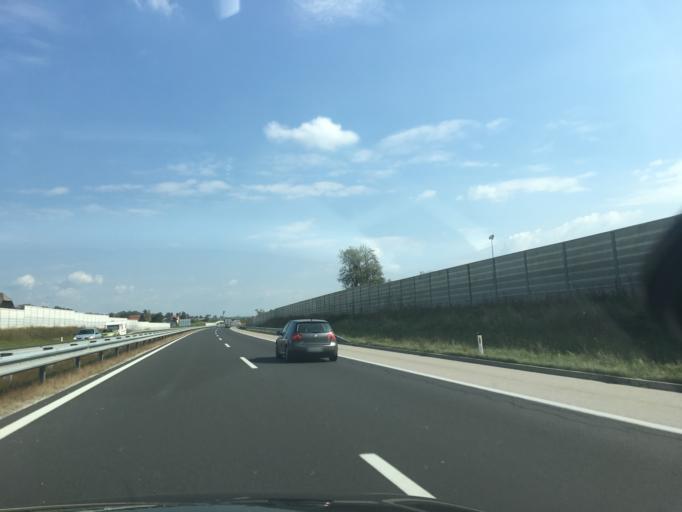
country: SI
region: Skocjan
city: Skocjan
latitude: 45.9074
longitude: 15.3595
